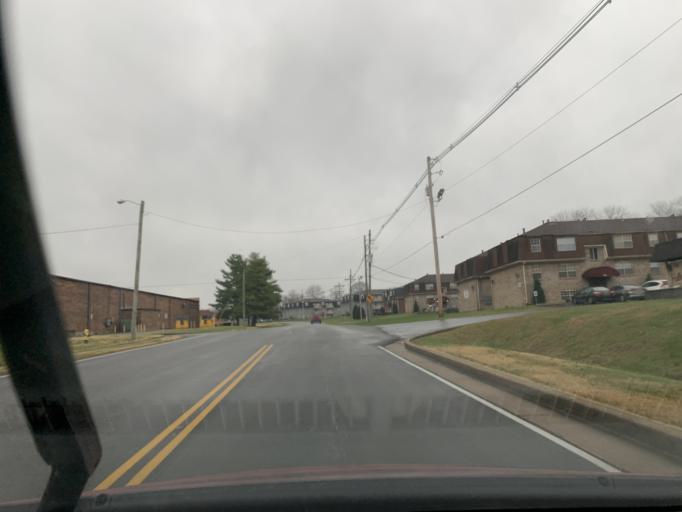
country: US
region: Kentucky
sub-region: Jefferson County
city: Buechel
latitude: 38.1977
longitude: -85.6241
